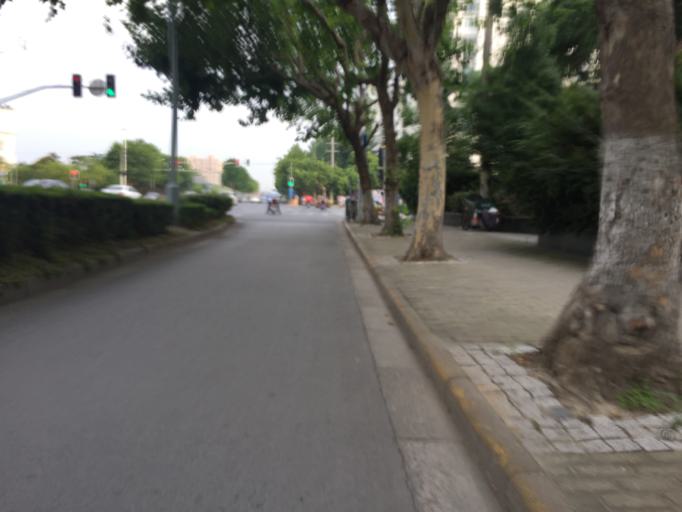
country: CN
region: Shanghai Shi
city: Huamu
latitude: 31.1825
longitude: 121.5374
